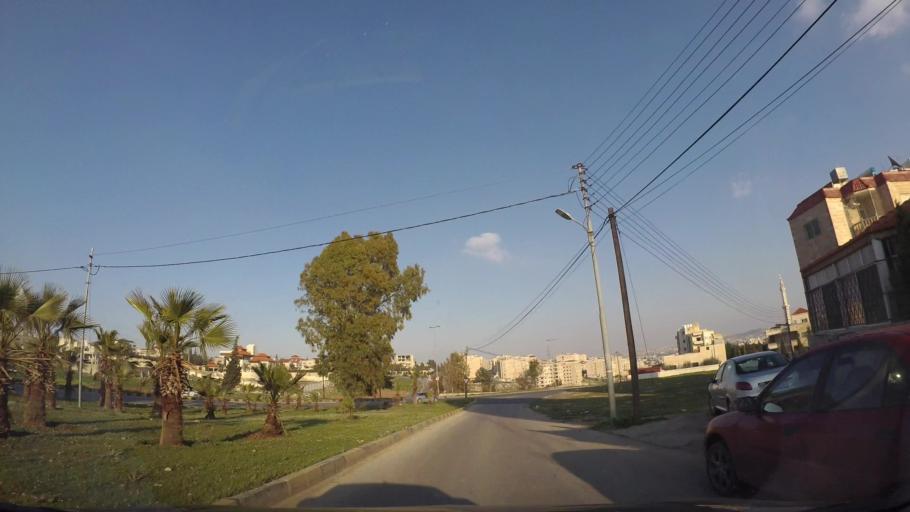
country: JO
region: Amman
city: Amman
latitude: 31.9858
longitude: 35.9513
